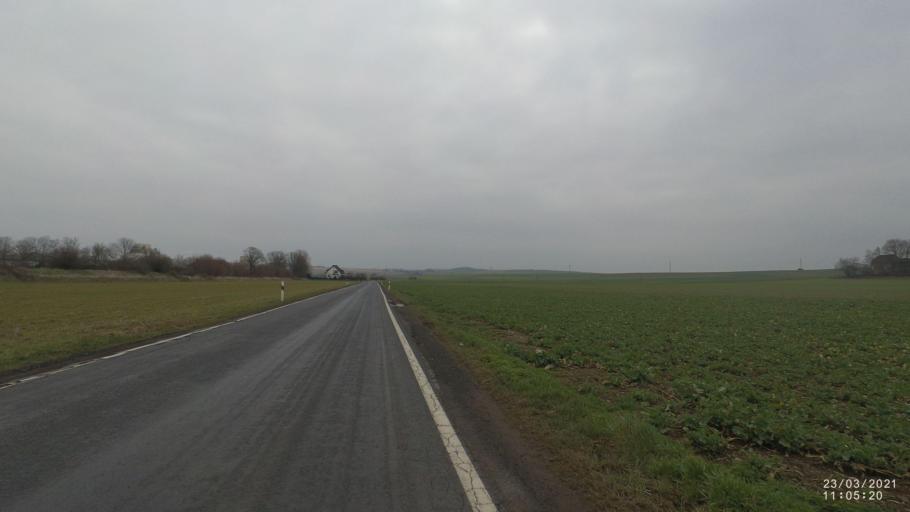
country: DE
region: Rheinland-Pfalz
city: Welling
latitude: 50.3554
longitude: 7.3125
